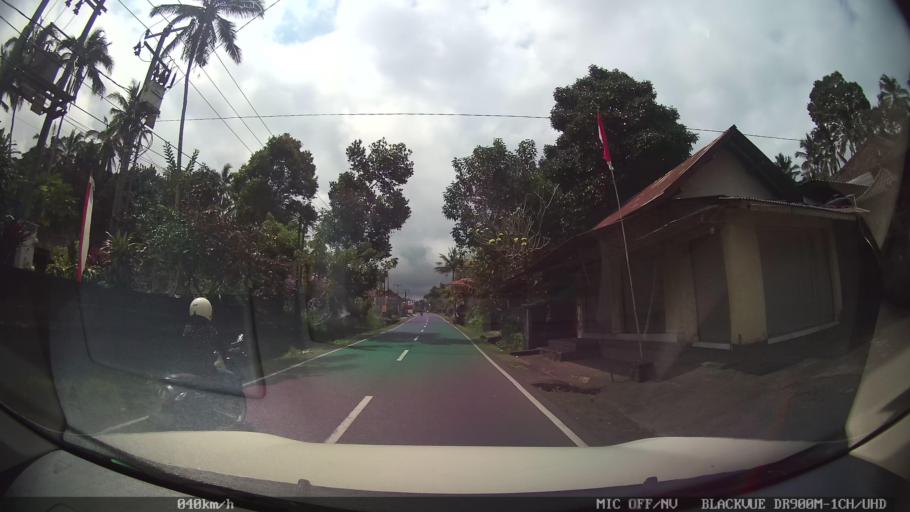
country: ID
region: Bali
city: Banjar Kubu
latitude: -8.4056
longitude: 115.4211
